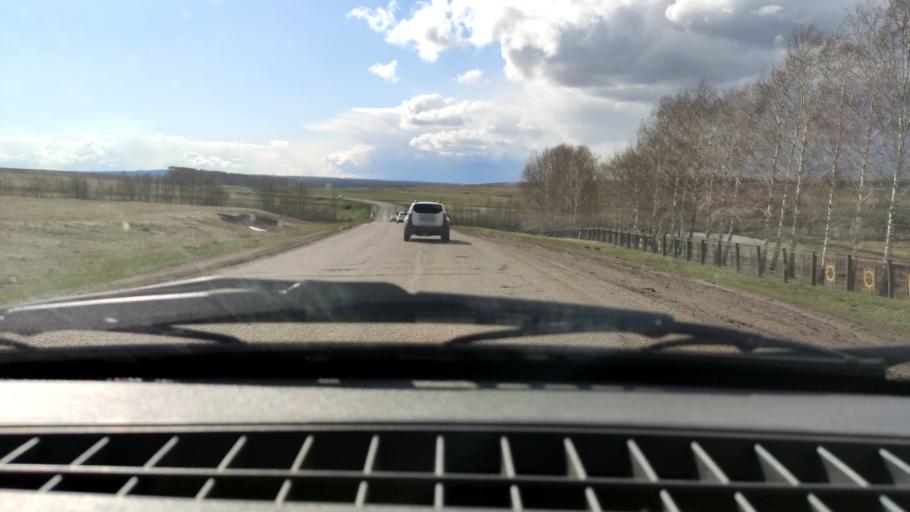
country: RU
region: Bashkortostan
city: Chekmagush
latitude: 55.1190
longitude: 54.7930
